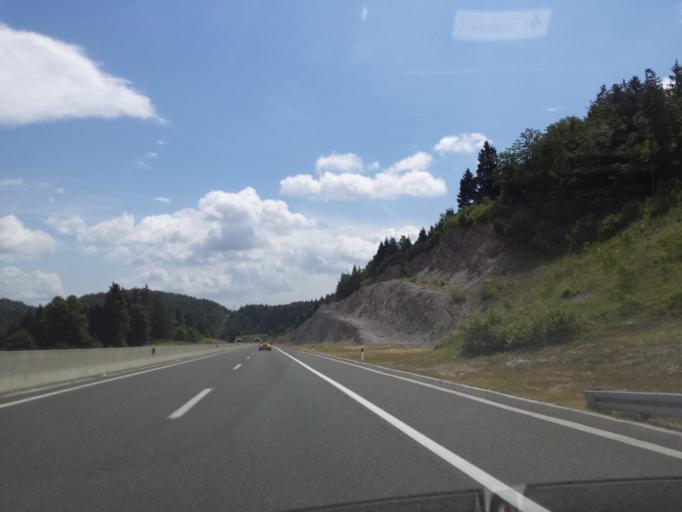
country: HR
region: Primorsko-Goranska
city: Vrbovsko
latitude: 45.3735
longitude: 14.9960
